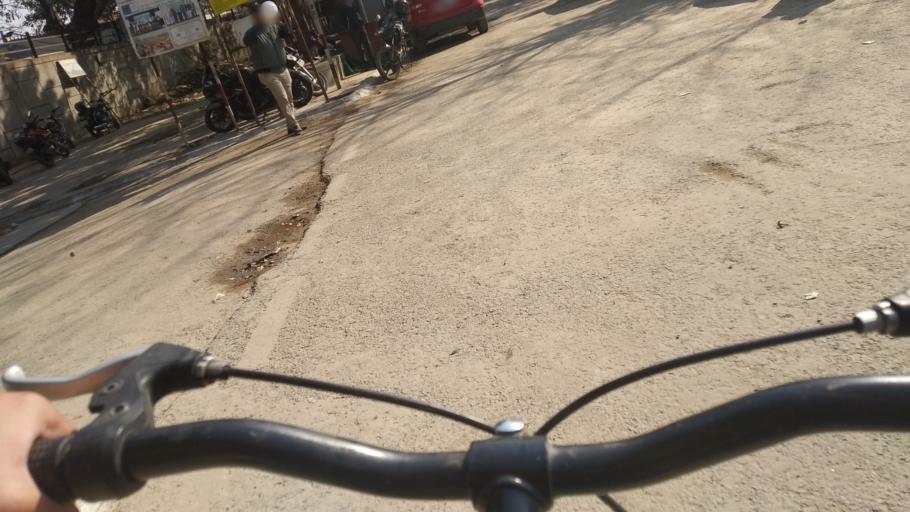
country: IN
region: NCT
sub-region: New Delhi
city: New Delhi
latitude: 28.6184
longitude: 77.2407
